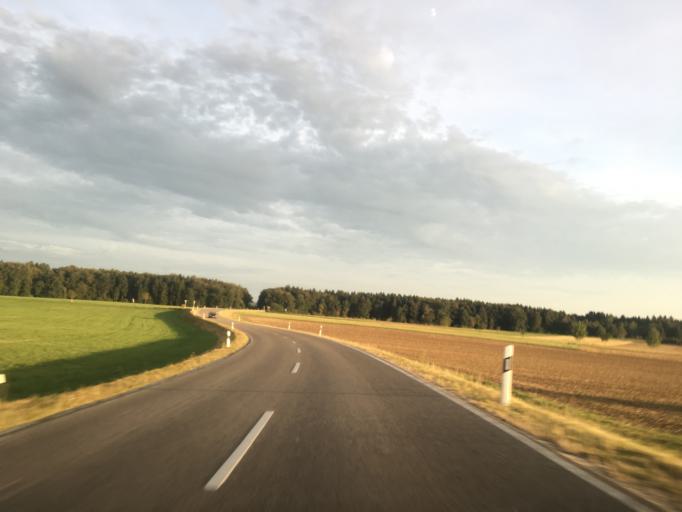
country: DE
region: Baden-Wuerttemberg
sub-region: Tuebingen Region
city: Hayingen
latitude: 48.3086
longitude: 9.4457
